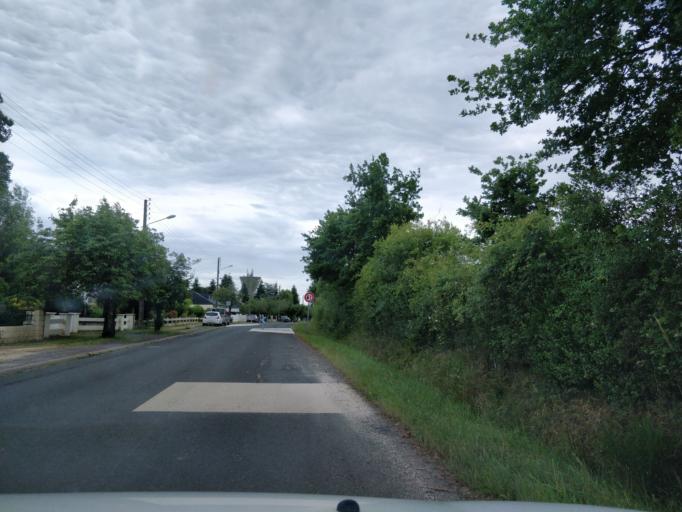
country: FR
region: Pays de la Loire
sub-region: Departement de Maine-et-Loire
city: Feneu
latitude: 47.5763
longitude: -0.5970
